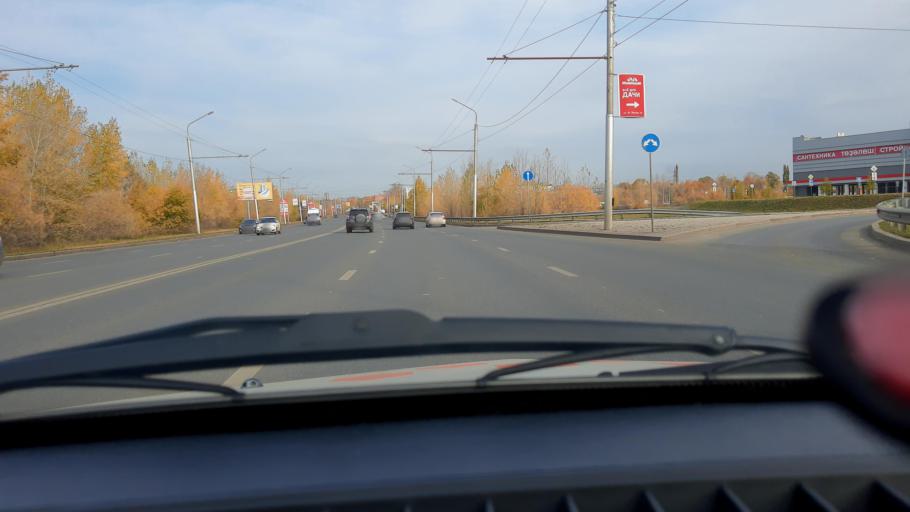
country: RU
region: Bashkortostan
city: Ufa
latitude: 54.7886
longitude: 56.0781
